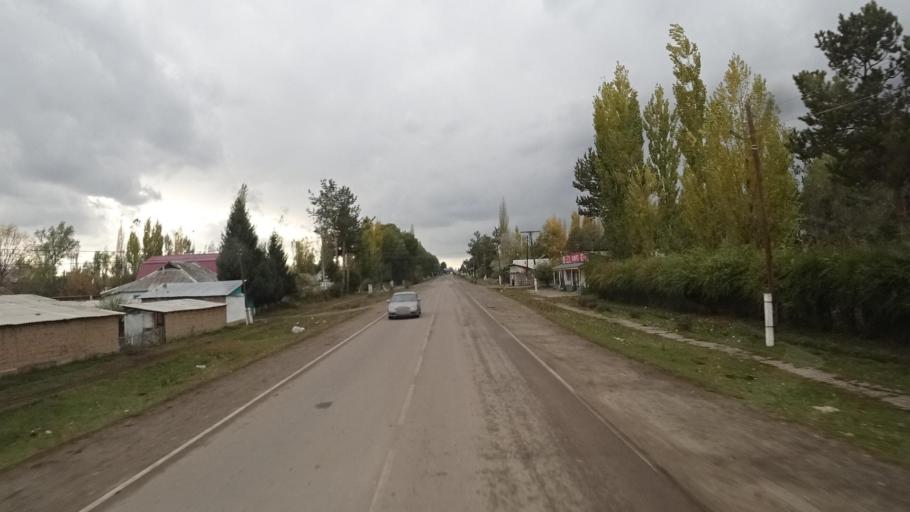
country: KG
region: Ysyk-Koel
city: Tyup
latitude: 42.7825
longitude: 78.5082
